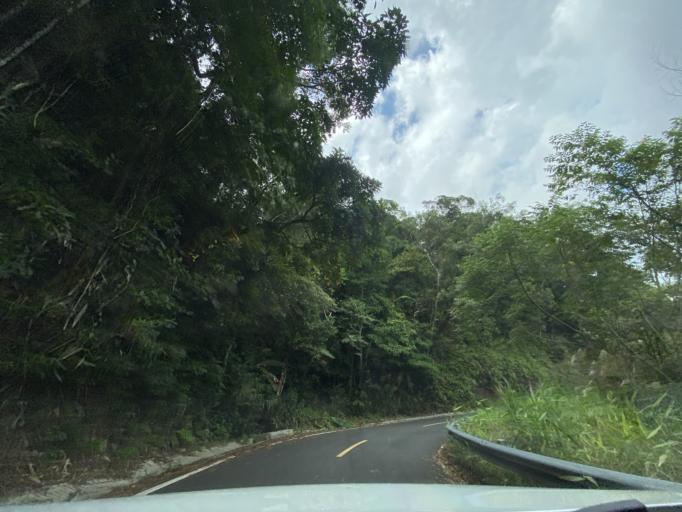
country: CN
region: Hainan
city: Benhao
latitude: 18.6857
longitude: 109.8791
